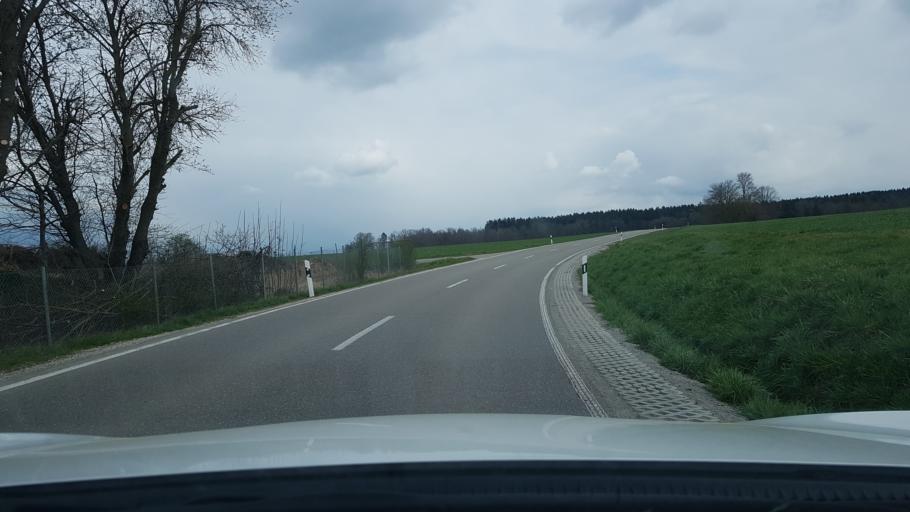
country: DE
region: Baden-Wuerttemberg
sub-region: Tuebingen Region
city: Oberstadion
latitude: 48.1795
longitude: 9.7359
